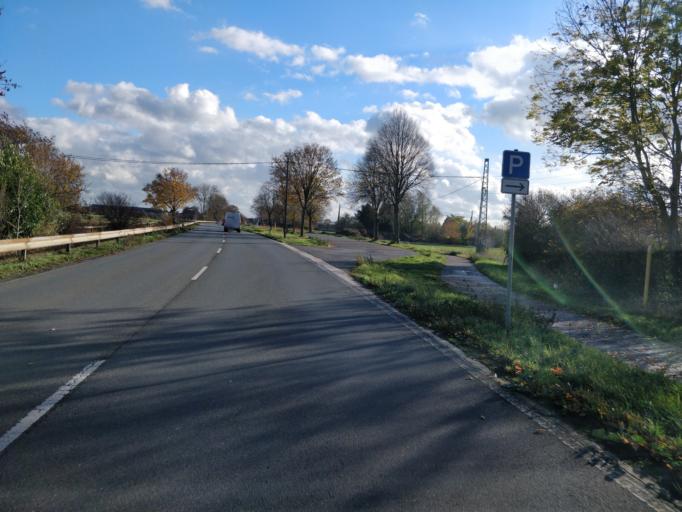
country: DE
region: North Rhine-Westphalia
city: Rees
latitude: 51.7788
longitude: 6.3776
